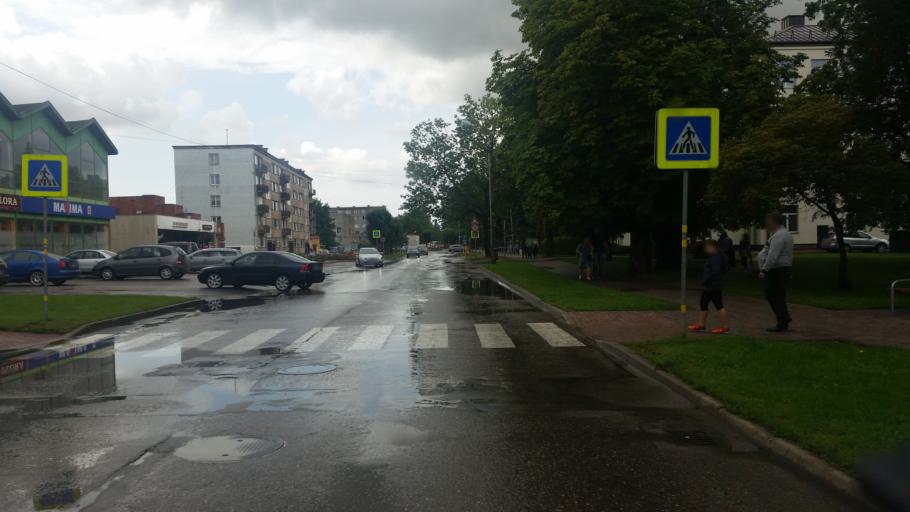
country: LV
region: Bauskas Rajons
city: Bauska
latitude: 56.4094
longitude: 24.1969
